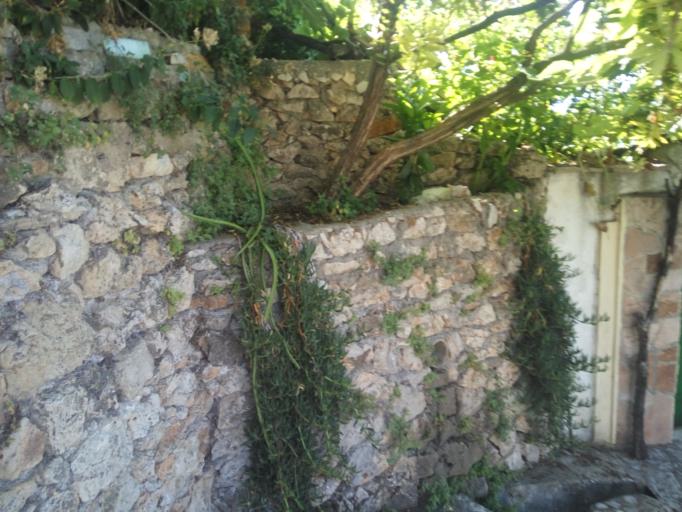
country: AL
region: Vlore
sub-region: Rrethi i Vlores
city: Himare
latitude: 40.0523
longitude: 19.8288
